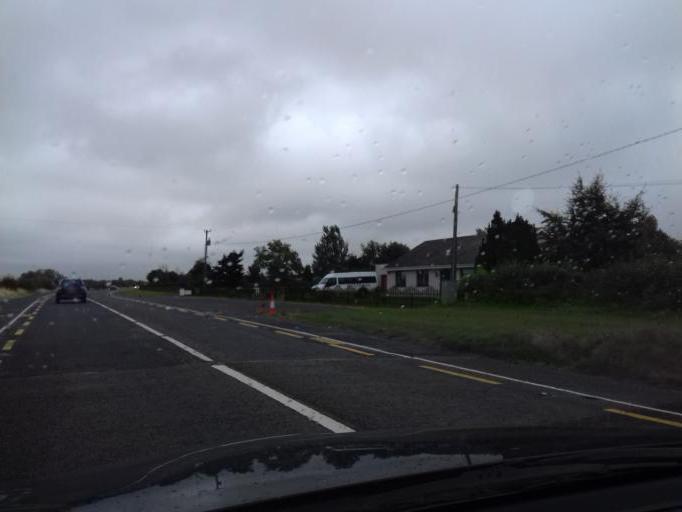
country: IE
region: Leinster
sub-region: County Carlow
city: Bagenalstown
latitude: 52.7475
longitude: -6.9672
